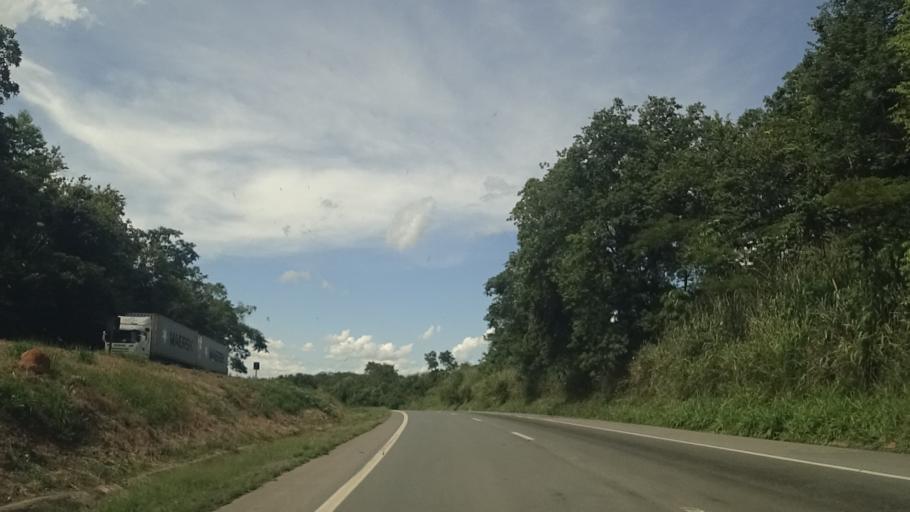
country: BR
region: Goias
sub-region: Piracanjuba
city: Piracanjuba
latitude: -17.2289
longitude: -49.2301
